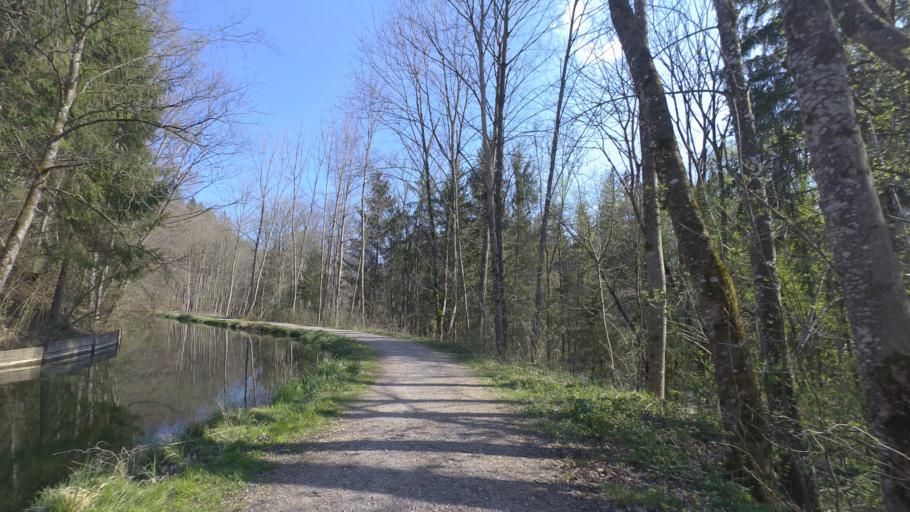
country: DE
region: Bavaria
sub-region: Upper Bavaria
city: Traunreut
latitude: 47.9617
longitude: 12.5737
